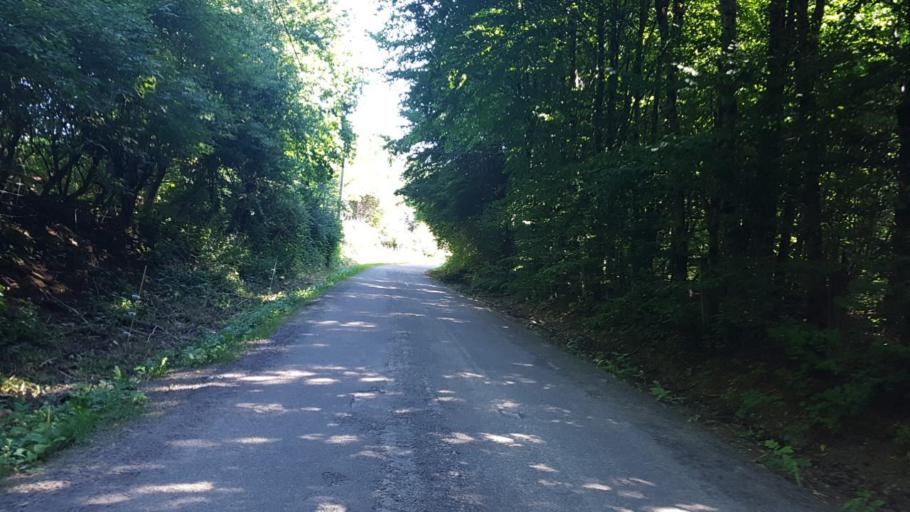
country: FR
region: Nord-Pas-de-Calais
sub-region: Departement du Nord
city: Anor
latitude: 49.9767
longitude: 4.1239
